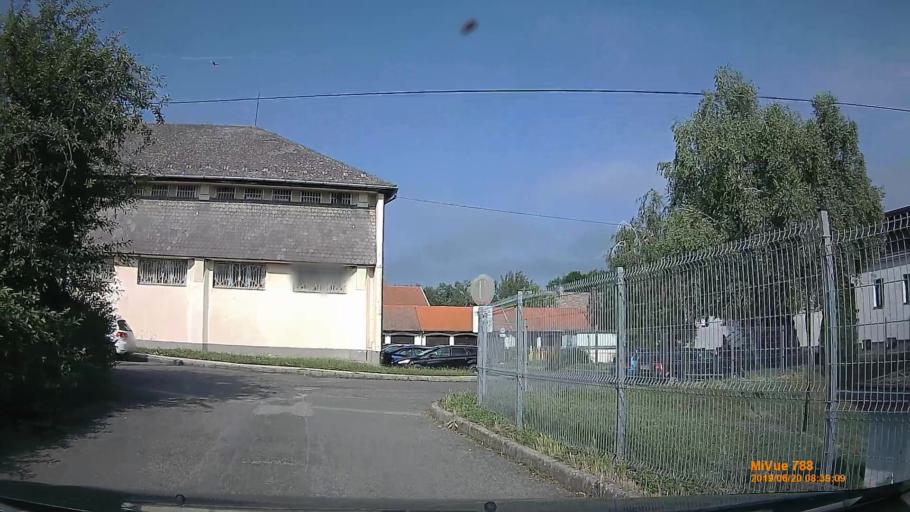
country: HU
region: Baranya
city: Szigetvar
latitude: 46.0489
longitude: 17.7998
